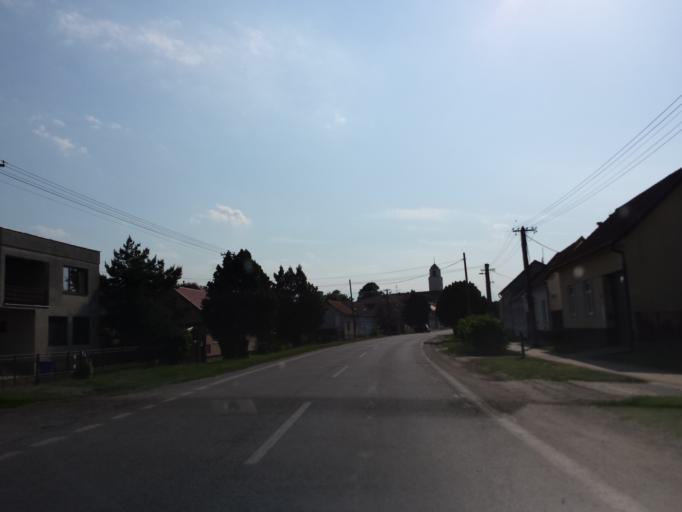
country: AT
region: Lower Austria
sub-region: Politischer Bezirk Ganserndorf
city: Angern an der March
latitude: 48.3822
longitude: 16.8526
